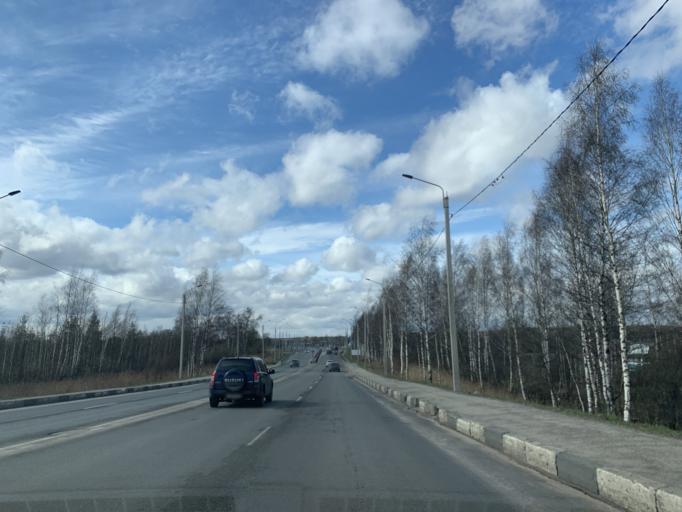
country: RU
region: Jaroslavl
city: Yaroslavl
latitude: 57.6673
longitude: 39.9507
